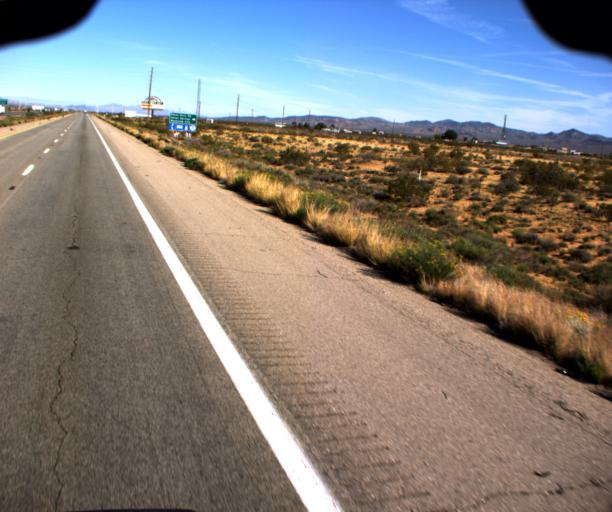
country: US
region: Arizona
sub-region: Mohave County
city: Dolan Springs
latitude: 35.5302
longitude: -114.3526
